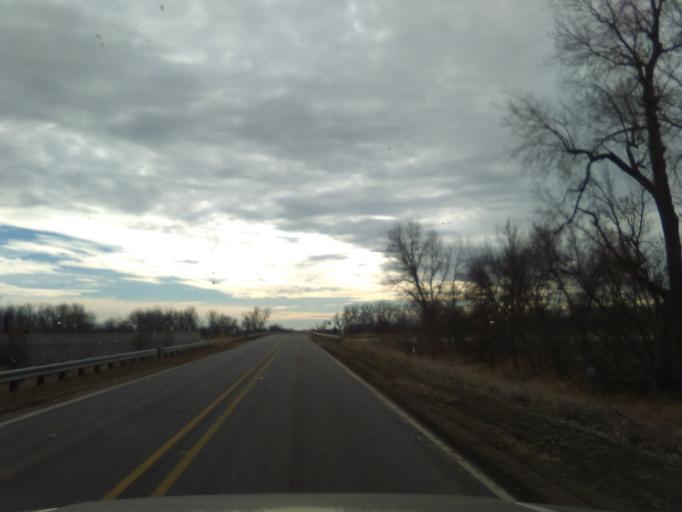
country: US
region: Nebraska
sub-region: Buffalo County
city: Shelton
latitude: 40.7178
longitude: -98.7407
